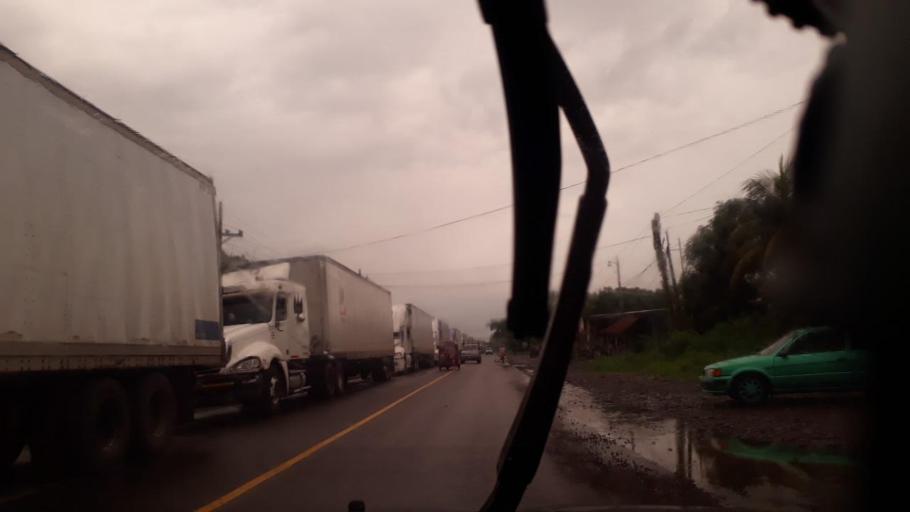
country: SV
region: Ahuachapan
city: San Francisco Menendez
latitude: 13.8807
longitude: -90.1022
